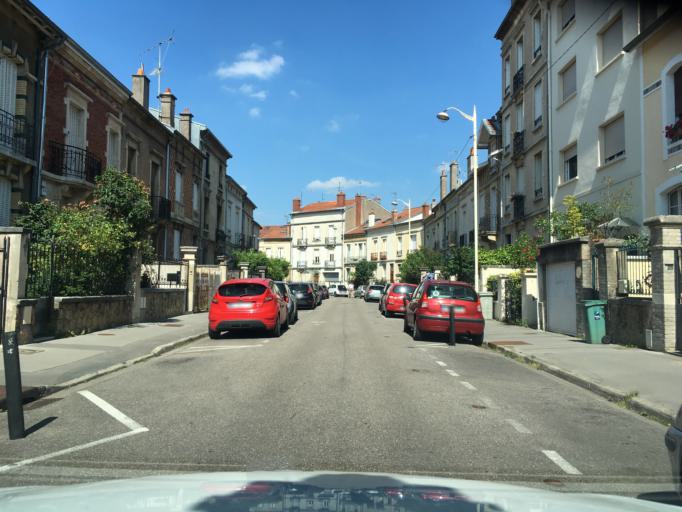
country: FR
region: Lorraine
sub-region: Departement de Meurthe-et-Moselle
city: Villers-les-Nancy
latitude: 48.6755
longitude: 6.1648
